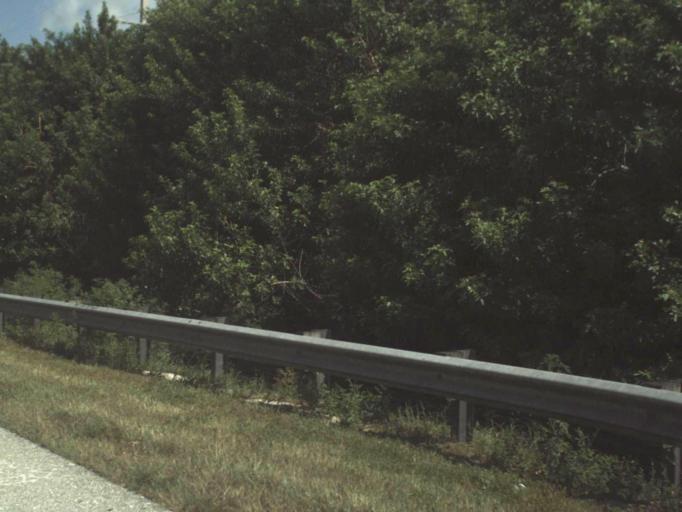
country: US
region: Florida
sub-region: Okeechobee County
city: Taylor Creek
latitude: 27.1314
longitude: -80.6355
